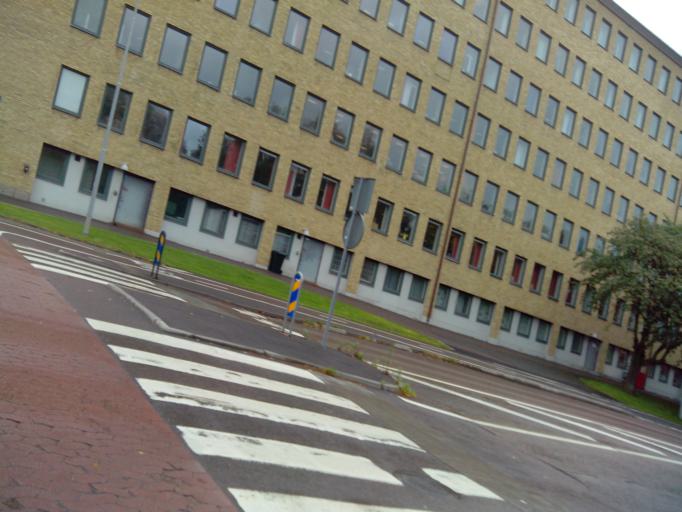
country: SE
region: Vaestra Goetaland
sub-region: Goteborg
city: Goeteborg
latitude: 57.7116
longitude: 11.9422
